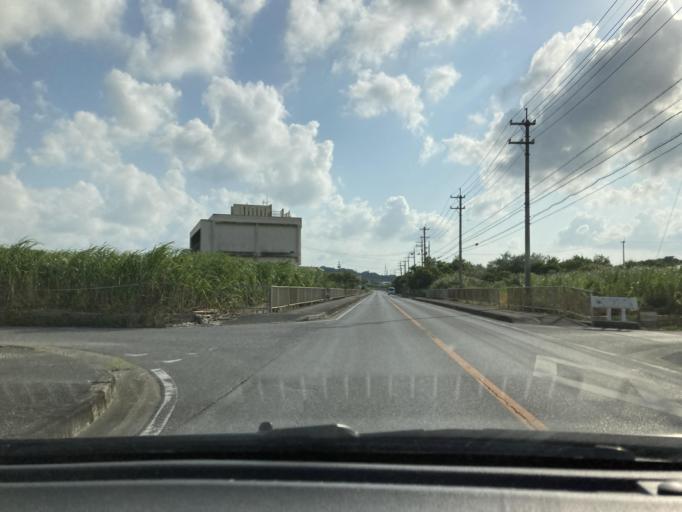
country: JP
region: Okinawa
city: Itoman
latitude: 26.1434
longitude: 127.7028
